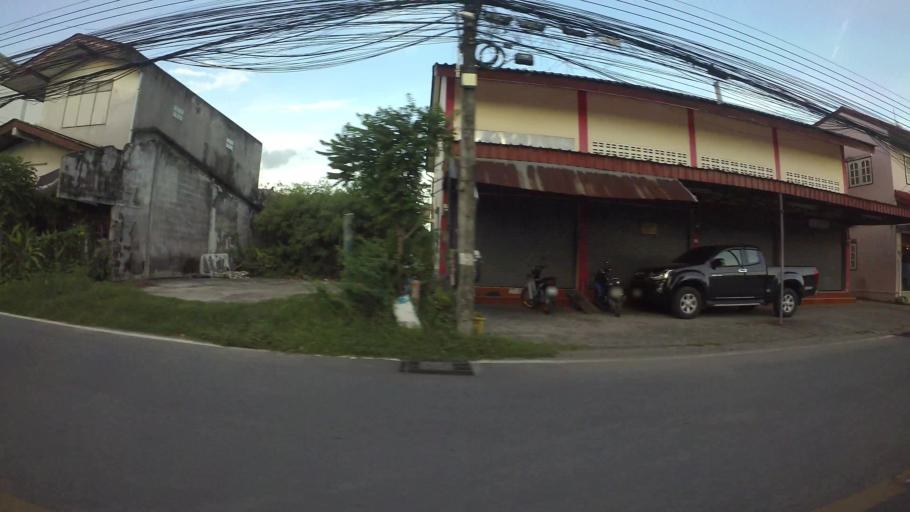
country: TH
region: Rayong
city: Rayong
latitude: 12.6826
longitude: 101.2845
